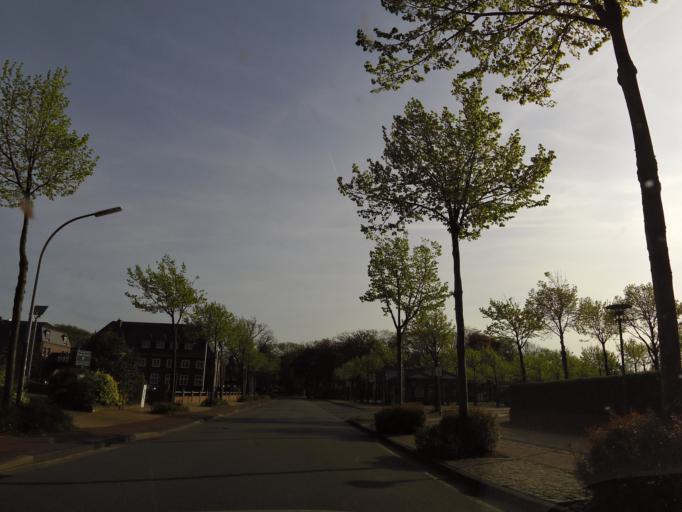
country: DE
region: Schleswig-Holstein
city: Niebull
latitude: 54.7886
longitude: 8.8264
